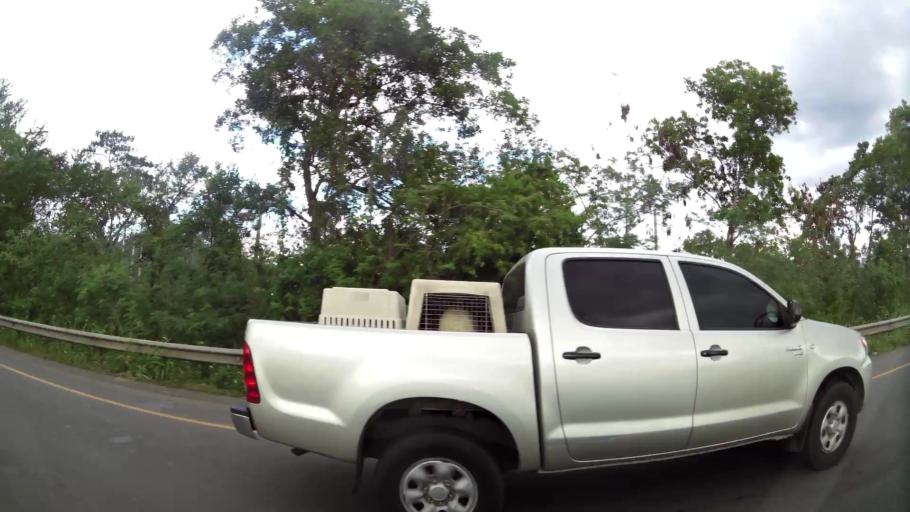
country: DO
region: Monsenor Nouel
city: Bonao
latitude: 18.9595
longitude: -70.4057
